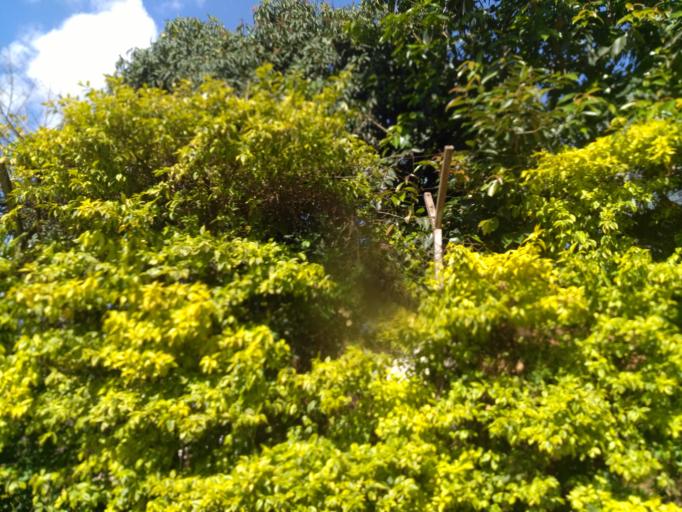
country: UG
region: Central Region
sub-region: Kampala District
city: Kampala
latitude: 0.3194
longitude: 32.5896
